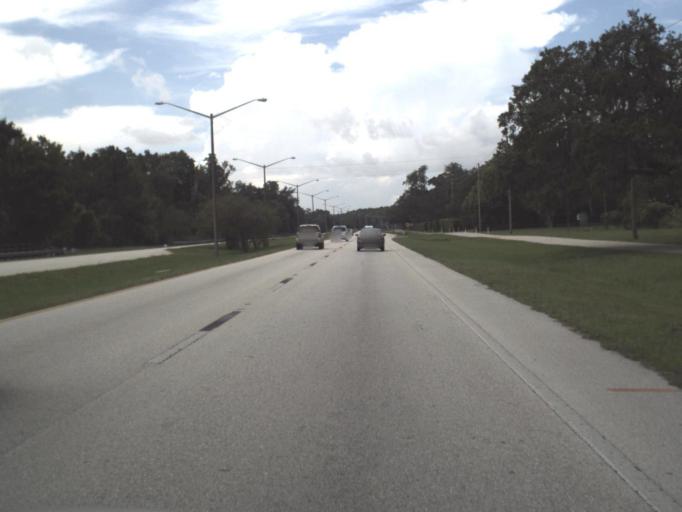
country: US
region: Florida
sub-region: Pinellas County
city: East Lake
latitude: 28.1241
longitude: -82.6964
